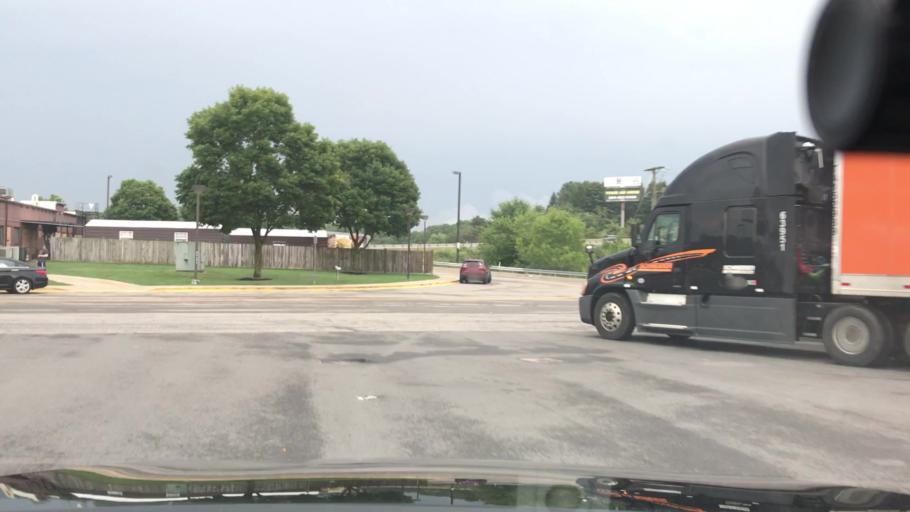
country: US
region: West Virginia
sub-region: Raleigh County
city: Mabscott
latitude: 37.8023
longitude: -81.2138
